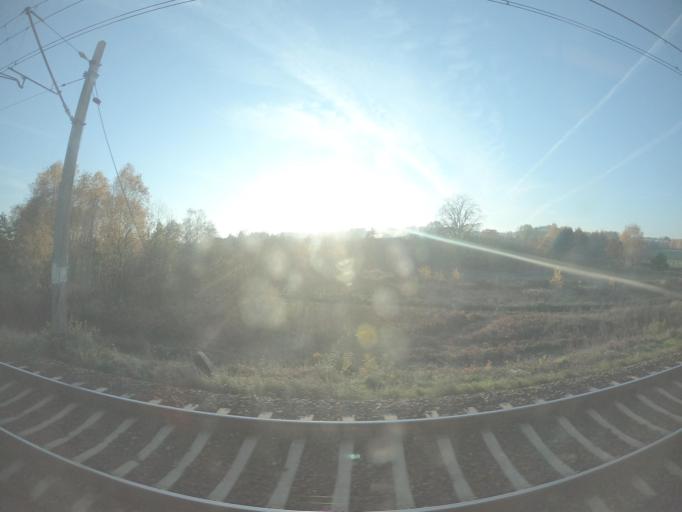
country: PL
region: Lubusz
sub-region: Powiat sulecinski
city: Torzym
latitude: 52.2561
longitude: 14.9502
